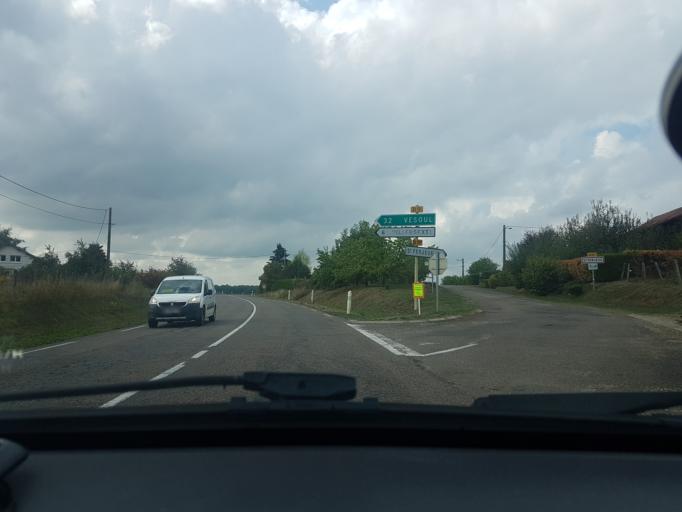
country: FR
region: Franche-Comte
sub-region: Departement de la Haute-Saone
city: Villersexel
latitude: 47.5428
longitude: 6.5140
